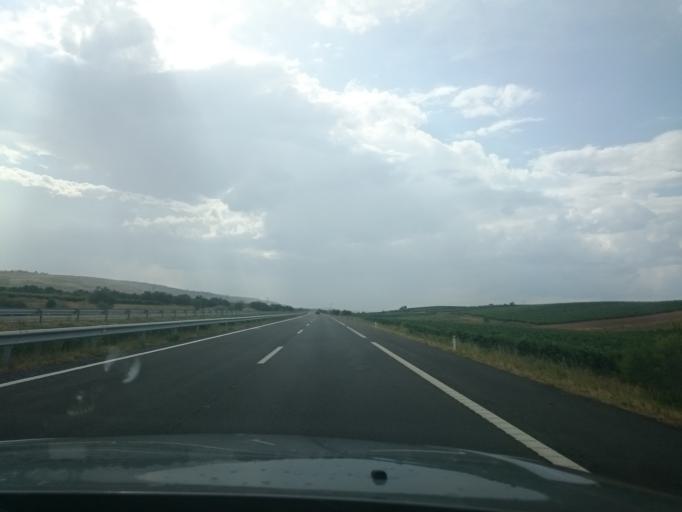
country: ES
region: La Rioja
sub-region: Provincia de La Rioja
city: Alcanadre
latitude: 42.3775
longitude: -2.0959
